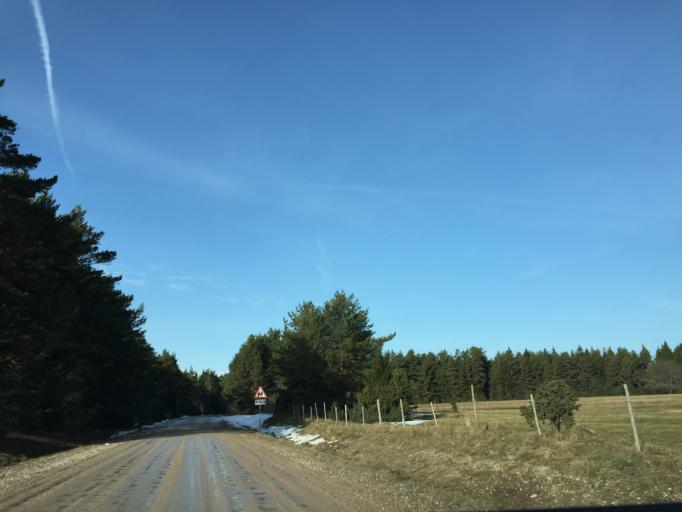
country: EE
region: Saare
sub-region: Kuressaare linn
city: Kuressaare
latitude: 58.3703
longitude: 22.0185
